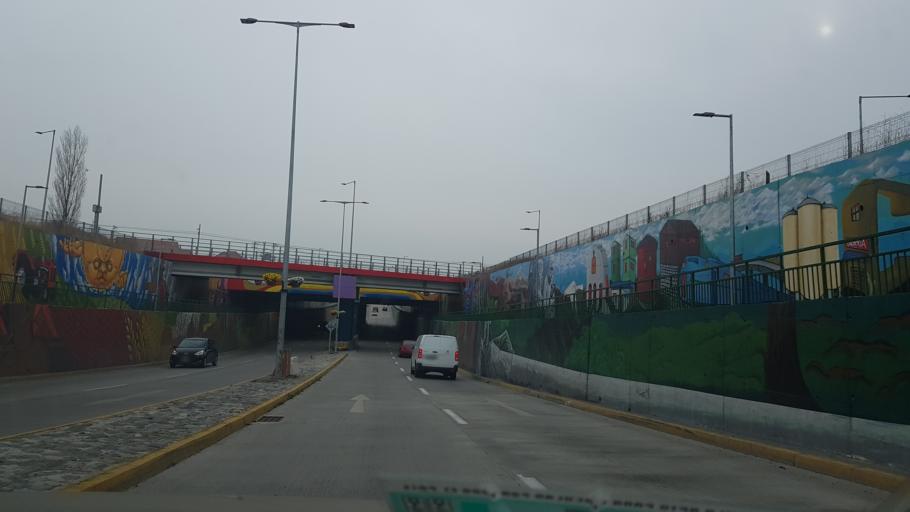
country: CL
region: Santiago Metropolitan
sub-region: Provincia de Santiago
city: Lo Prado
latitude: -33.3563
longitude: -70.7105
